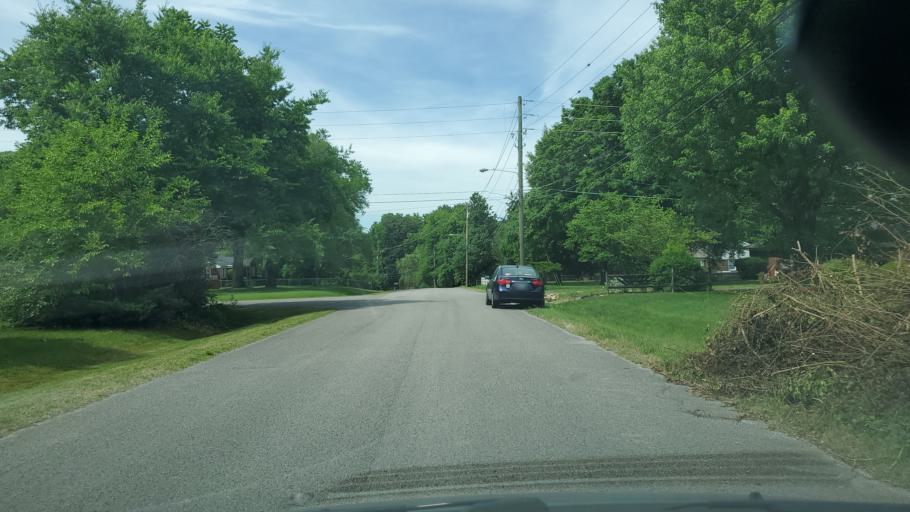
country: US
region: Tennessee
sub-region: Davidson County
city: Oak Hill
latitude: 36.1115
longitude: -86.6951
